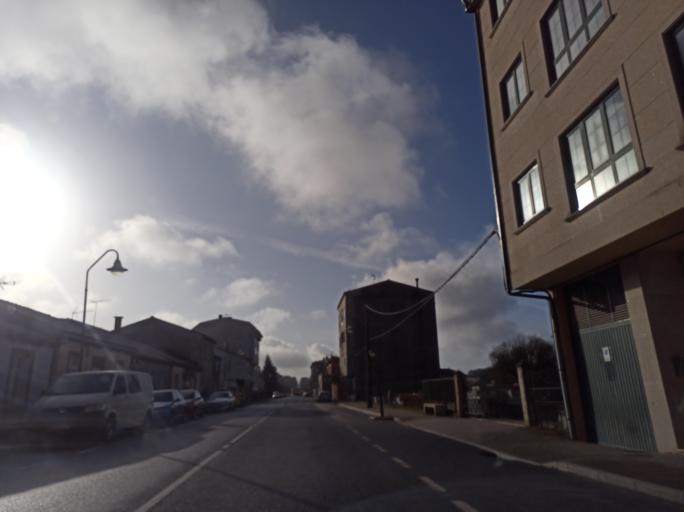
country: ES
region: Galicia
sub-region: Provincia da Coruna
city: Curtis
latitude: 43.1373
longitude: -8.0357
